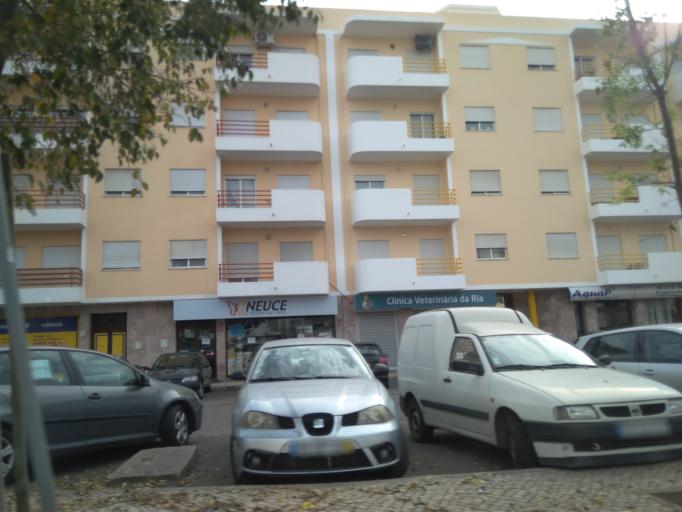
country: PT
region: Faro
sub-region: Olhao
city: Olhao
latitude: 37.0314
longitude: -7.8478
